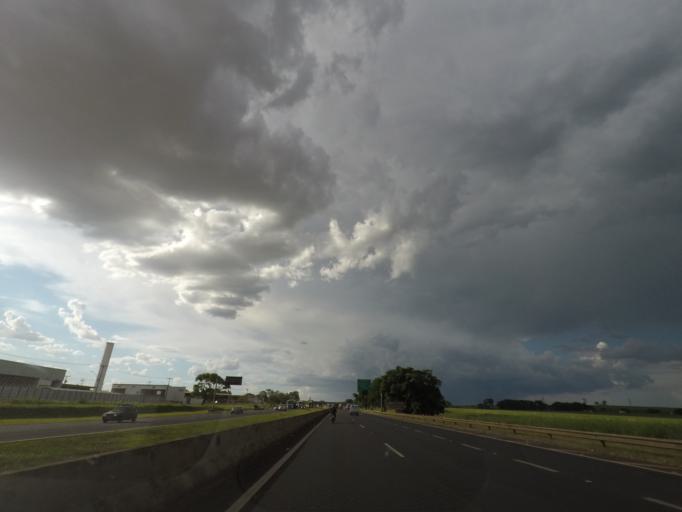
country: BR
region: Sao Paulo
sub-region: Ribeirao Preto
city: Ribeirao Preto
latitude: -21.1184
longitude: -47.7761
